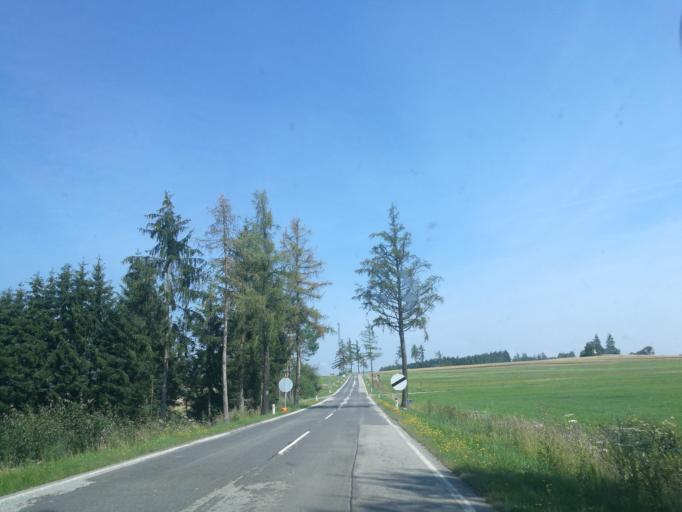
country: AT
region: Lower Austria
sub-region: Politischer Bezirk Gmund
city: Eisgarn
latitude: 48.9197
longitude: 15.1042
